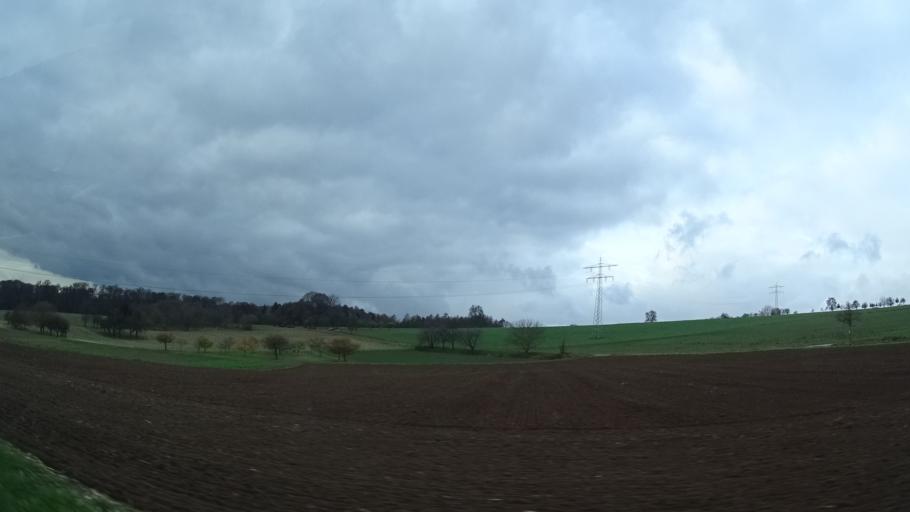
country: DE
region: Baden-Wuerttemberg
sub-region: Karlsruhe Region
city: Neckargerach
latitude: 49.4111
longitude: 9.0888
